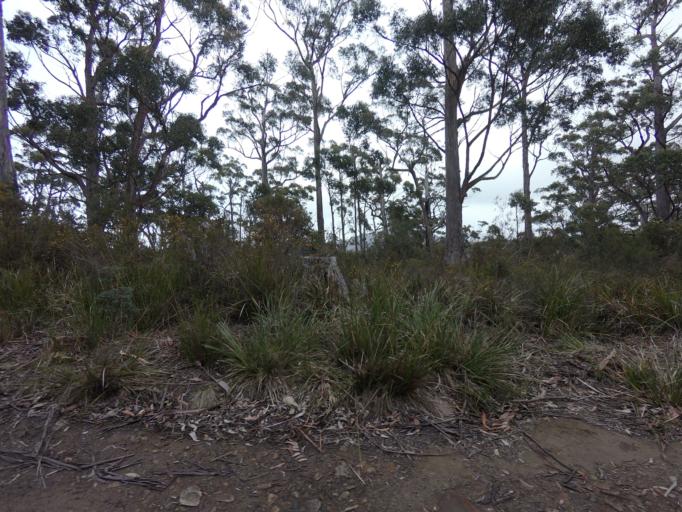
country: AU
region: Tasmania
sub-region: Huon Valley
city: Geeveston
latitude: -43.4754
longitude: 146.9340
